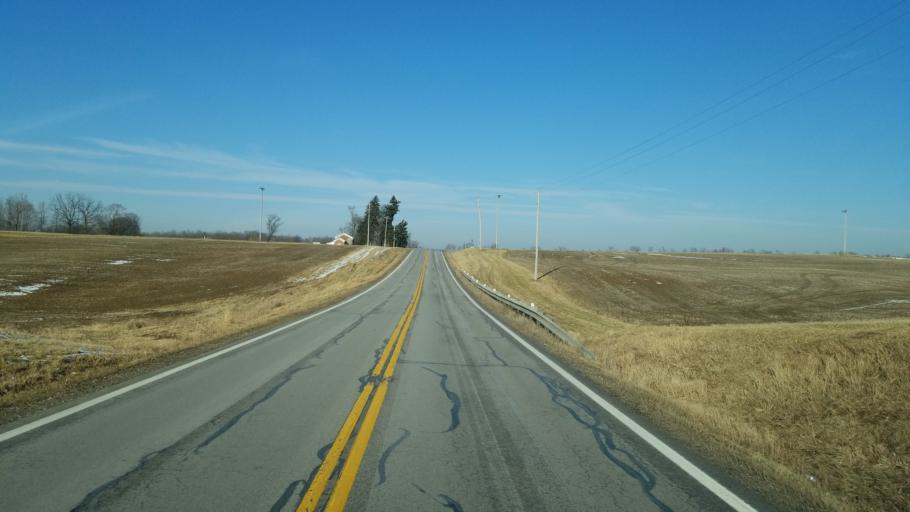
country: US
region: Ohio
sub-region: Huron County
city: Willard
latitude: 41.1174
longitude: -82.6611
